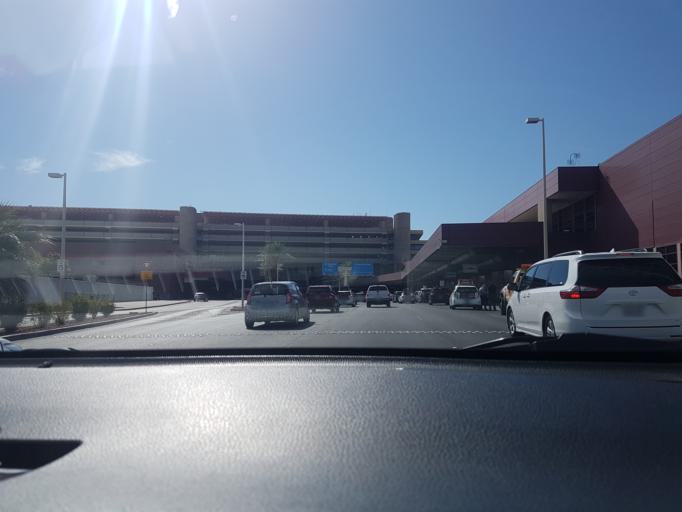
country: US
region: Nevada
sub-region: Clark County
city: Paradise
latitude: 36.0872
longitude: -115.1509
